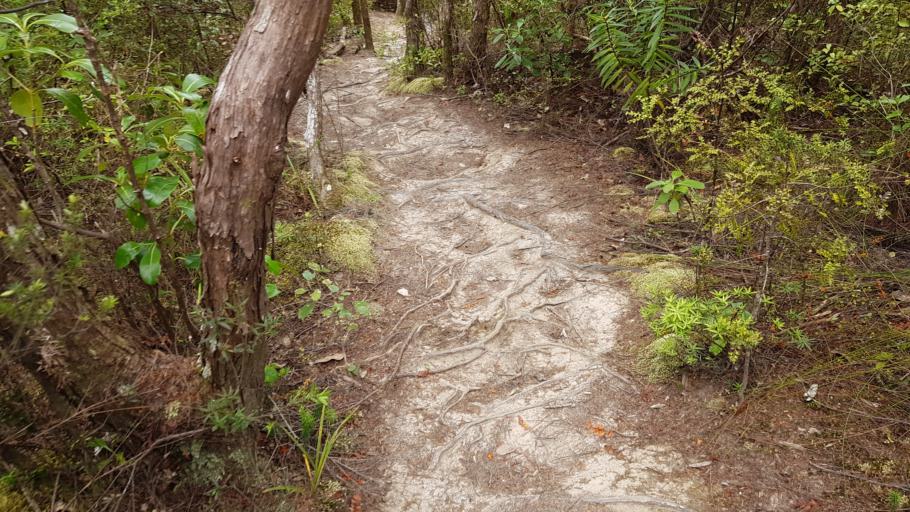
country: NZ
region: Auckland
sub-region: Auckland
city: North Shore
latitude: -36.8235
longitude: 174.7066
